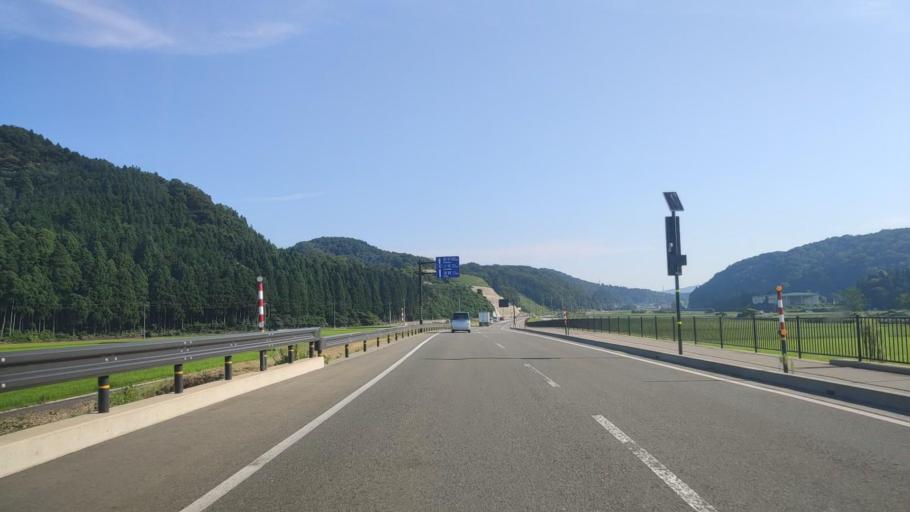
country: JP
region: Fukui
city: Maruoka
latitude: 36.2034
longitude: 136.2677
